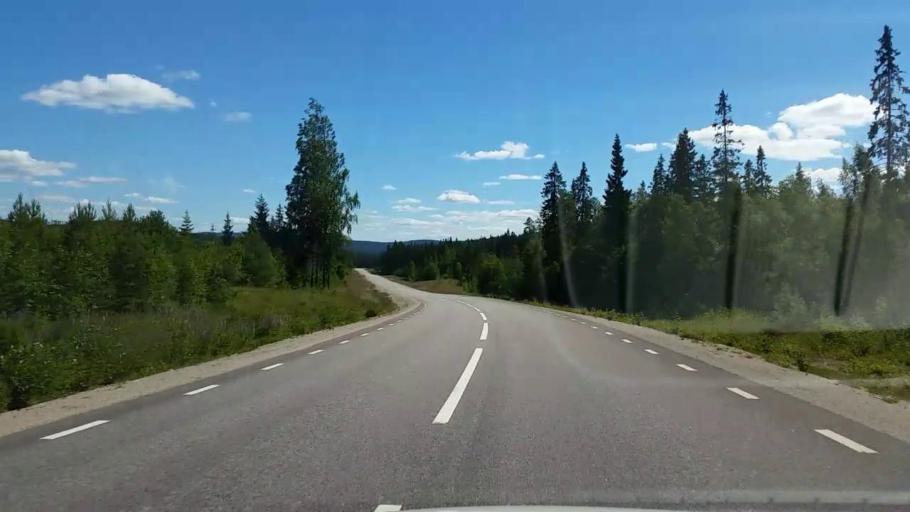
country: SE
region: Gaevleborg
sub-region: Bollnas Kommun
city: Vittsjo
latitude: 61.0688
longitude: 15.7958
